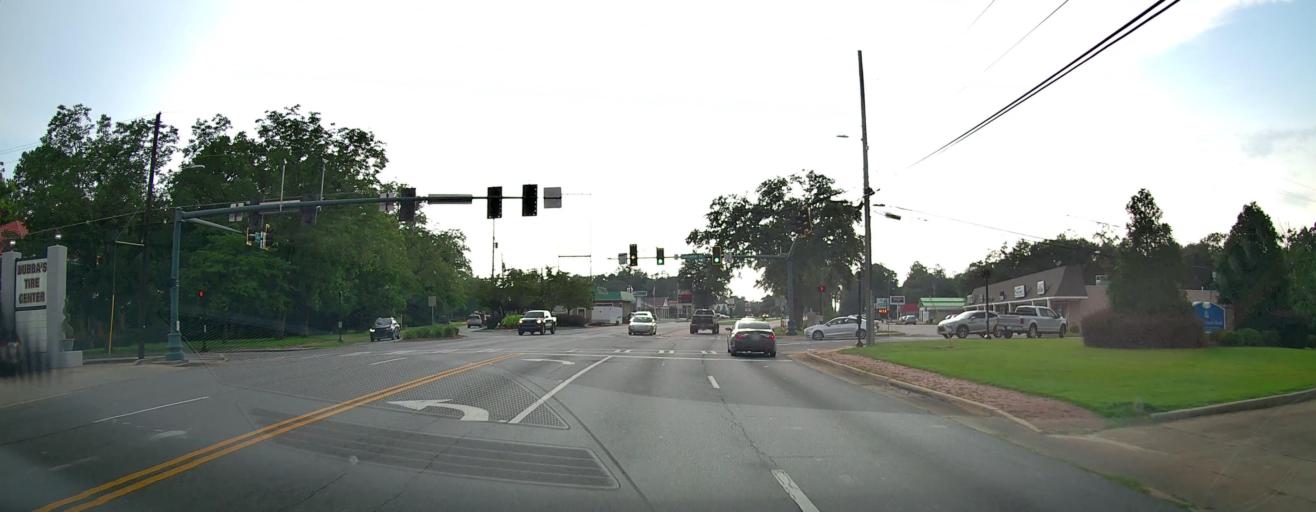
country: US
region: Georgia
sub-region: Laurens County
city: Dublin
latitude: 32.5356
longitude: -82.9257
